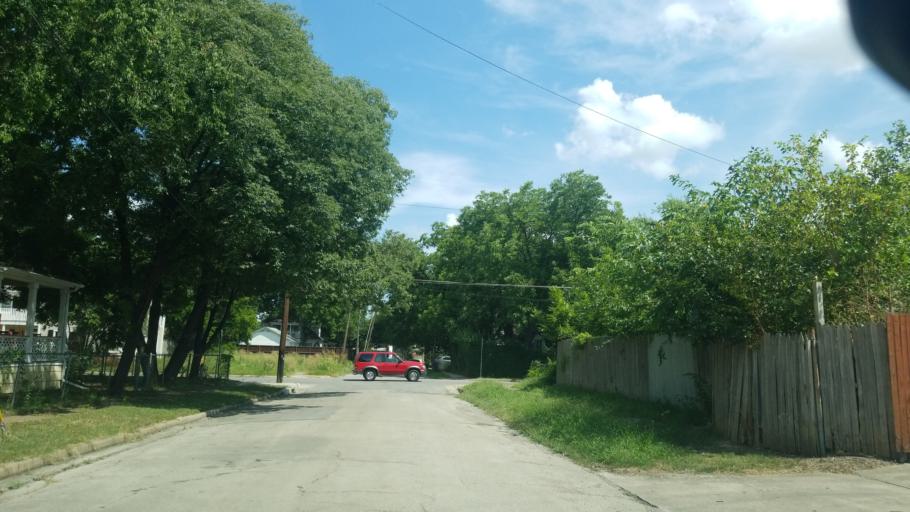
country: US
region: Texas
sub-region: Dallas County
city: Dallas
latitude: 32.8001
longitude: -96.7746
